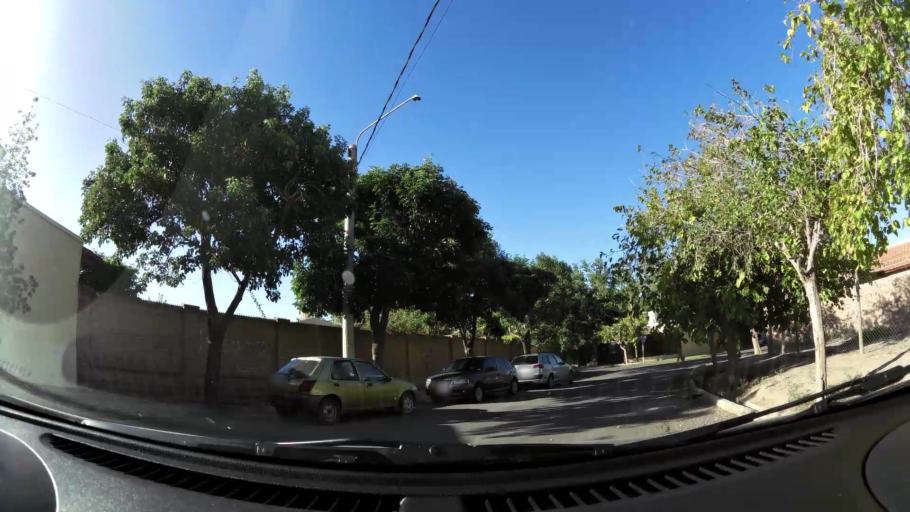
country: AR
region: San Juan
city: Villa Krause
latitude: -31.5610
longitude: -68.5171
